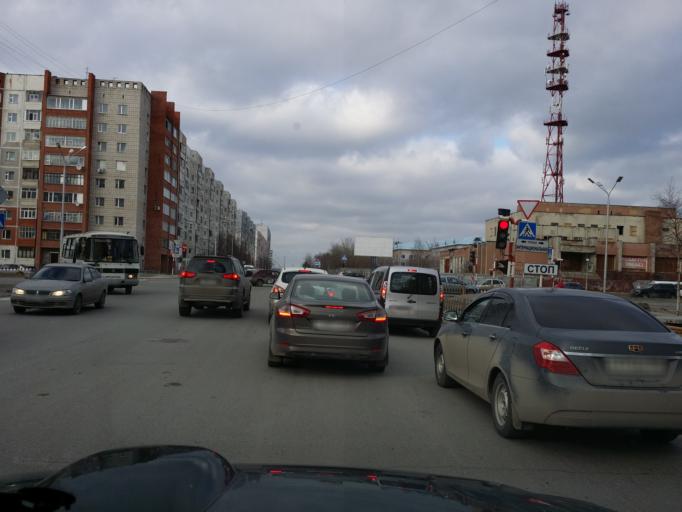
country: RU
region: Khanty-Mansiyskiy Avtonomnyy Okrug
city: Nizhnevartovsk
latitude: 60.9424
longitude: 76.6095
